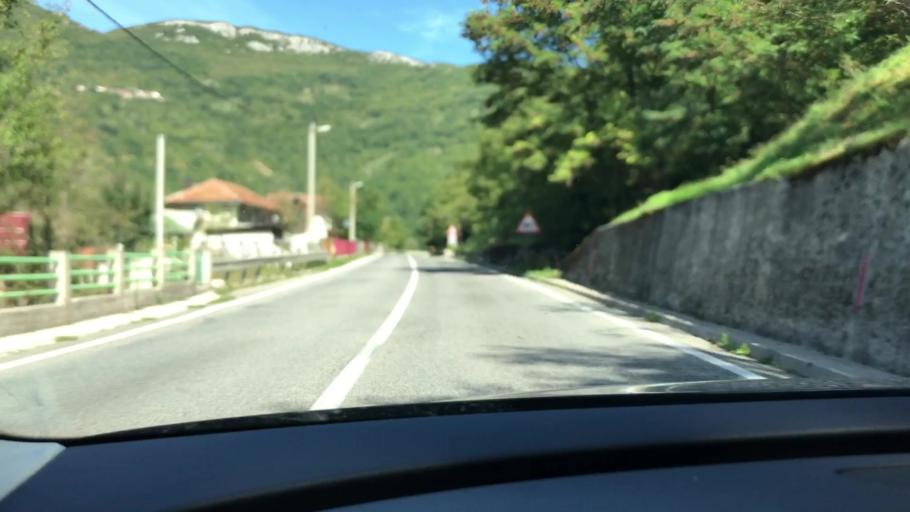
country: BA
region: Federation of Bosnia and Herzegovina
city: Jablanica
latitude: 43.6832
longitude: 17.7870
